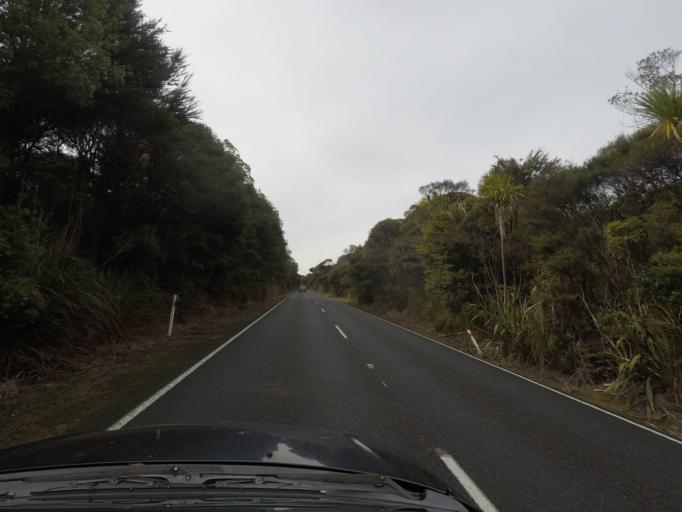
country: NZ
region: Auckland
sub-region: Auckland
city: Titirangi
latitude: -36.9350
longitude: 174.5628
